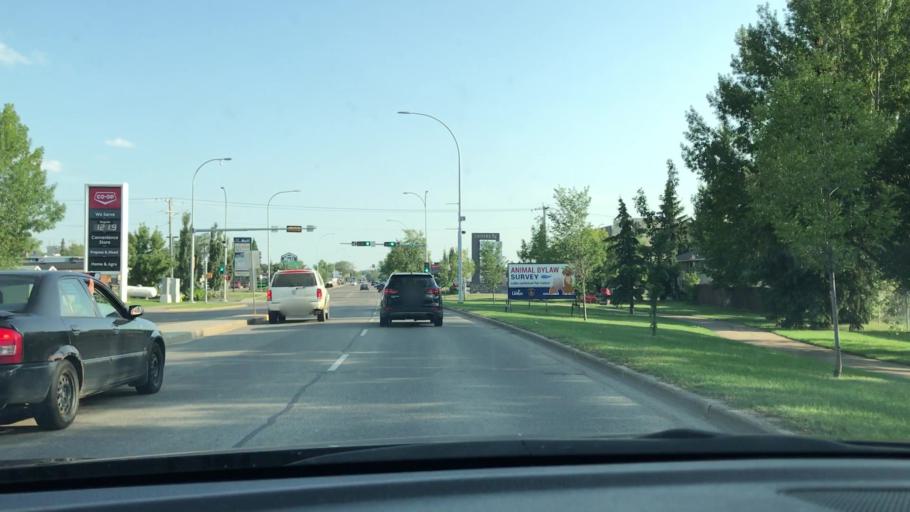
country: CA
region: Alberta
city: Leduc
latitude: 53.2691
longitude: -113.5525
